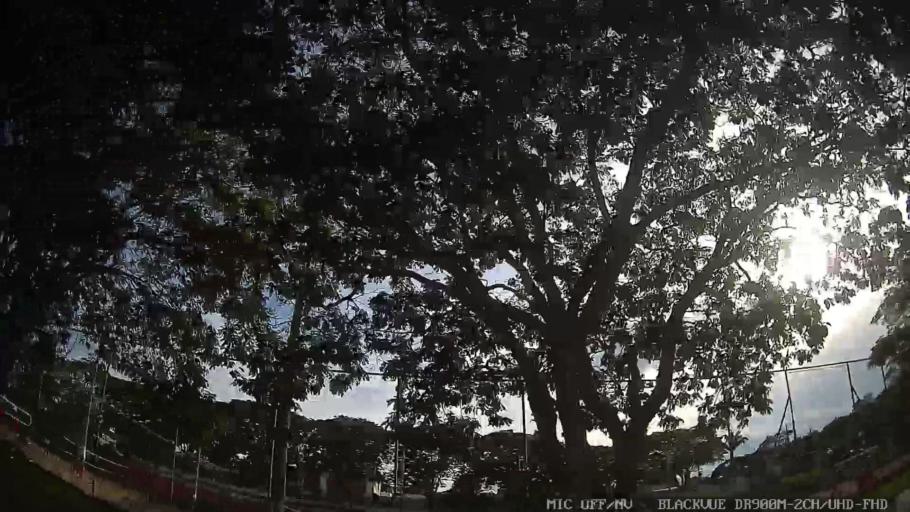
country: BR
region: Sao Paulo
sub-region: Jaguariuna
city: Jaguariuna
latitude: -22.6390
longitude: -47.0484
